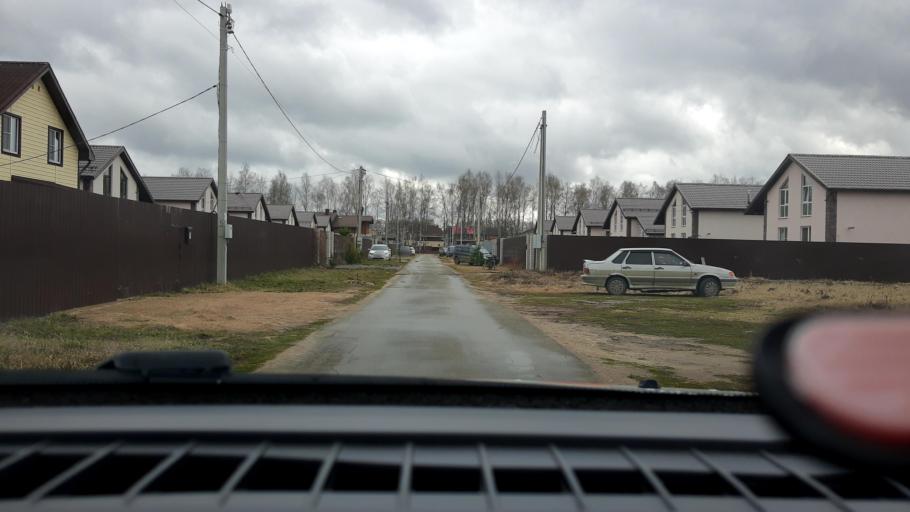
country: RU
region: Nizjnij Novgorod
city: Neklyudovo
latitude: 56.4104
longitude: 44.0215
